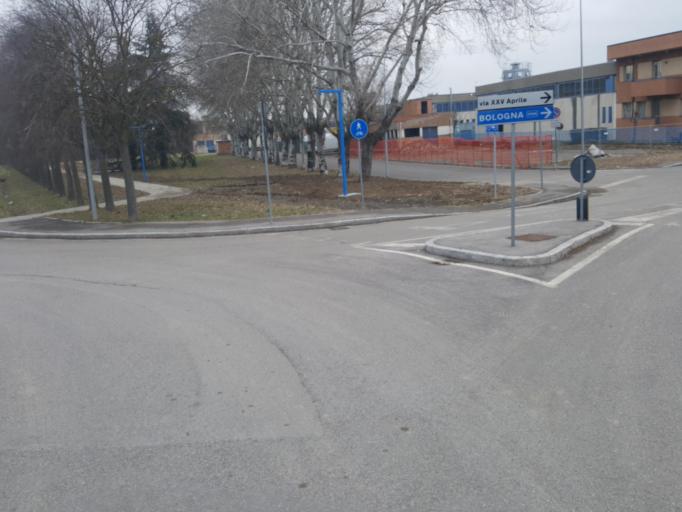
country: IT
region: Emilia-Romagna
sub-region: Provincia di Bologna
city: Calderara di Reno
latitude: 44.5444
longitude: 11.2619
